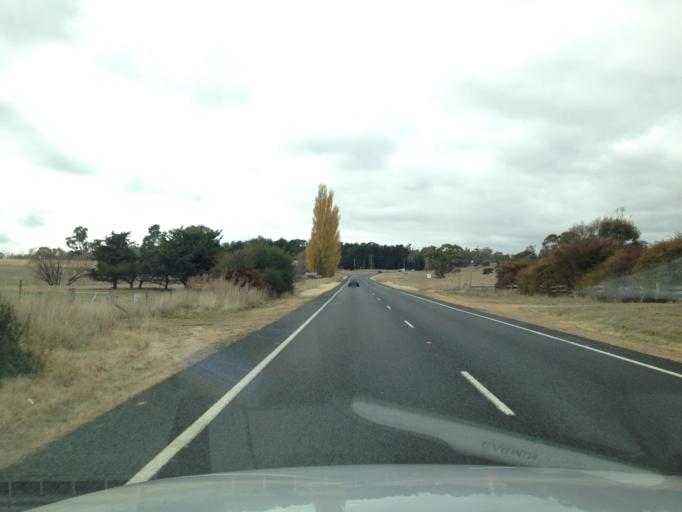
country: AU
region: New South Wales
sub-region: Cooma-Monaro
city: Cooma
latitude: -36.2427
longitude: 149.0628
